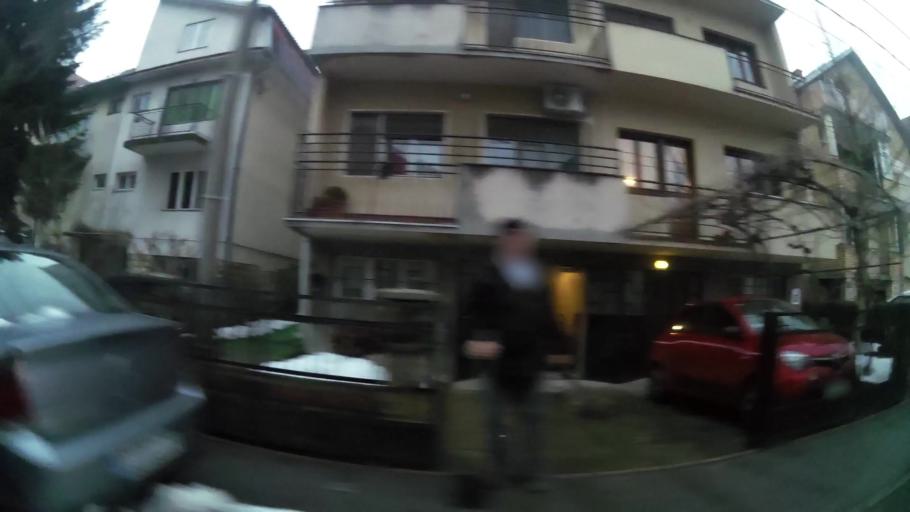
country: RS
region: Central Serbia
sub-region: Belgrade
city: Cukarica
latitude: 44.7602
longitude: 20.4224
